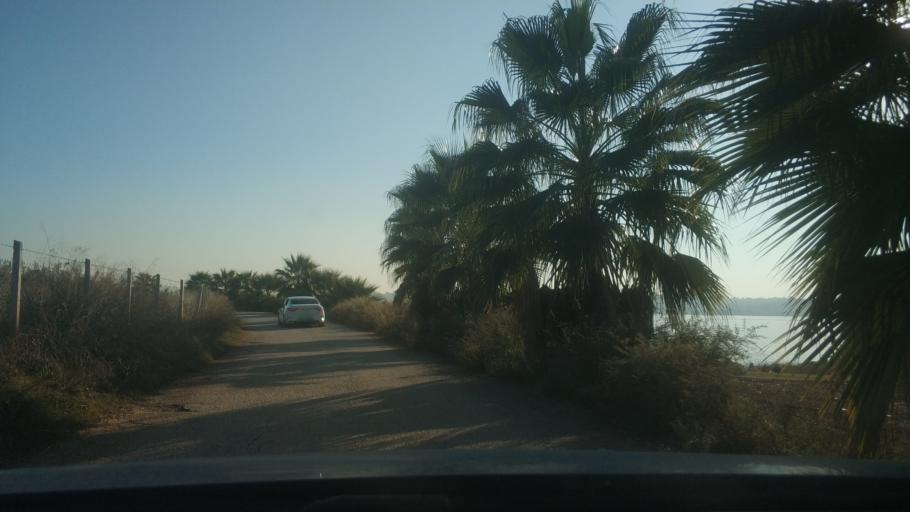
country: TR
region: Adana
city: Adana
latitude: 37.0912
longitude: 35.3012
